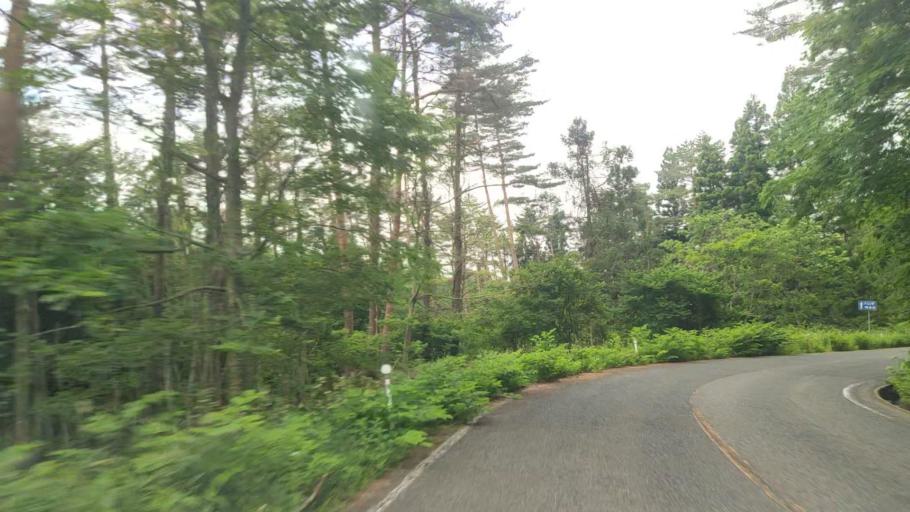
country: JP
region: Tottori
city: Yonago
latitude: 35.3297
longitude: 133.5696
